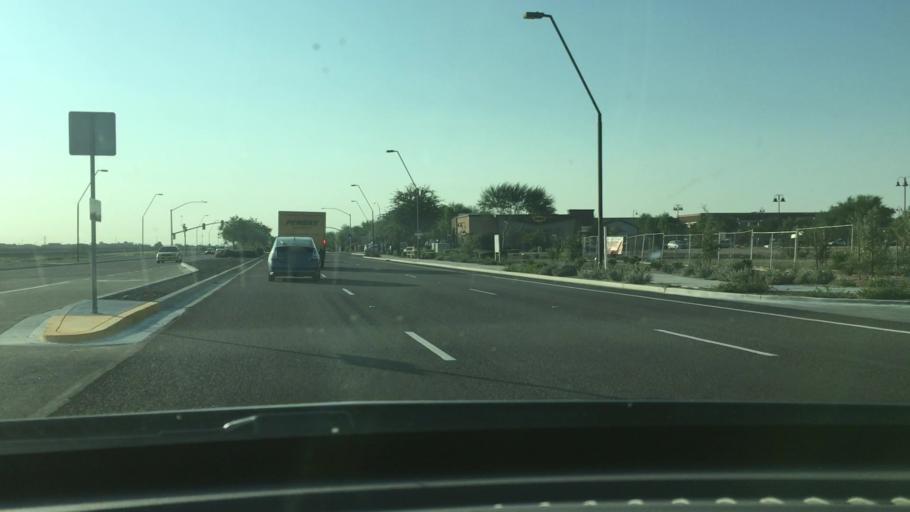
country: US
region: Arizona
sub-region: Maricopa County
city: Queen Creek
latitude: 33.2540
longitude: -111.6316
